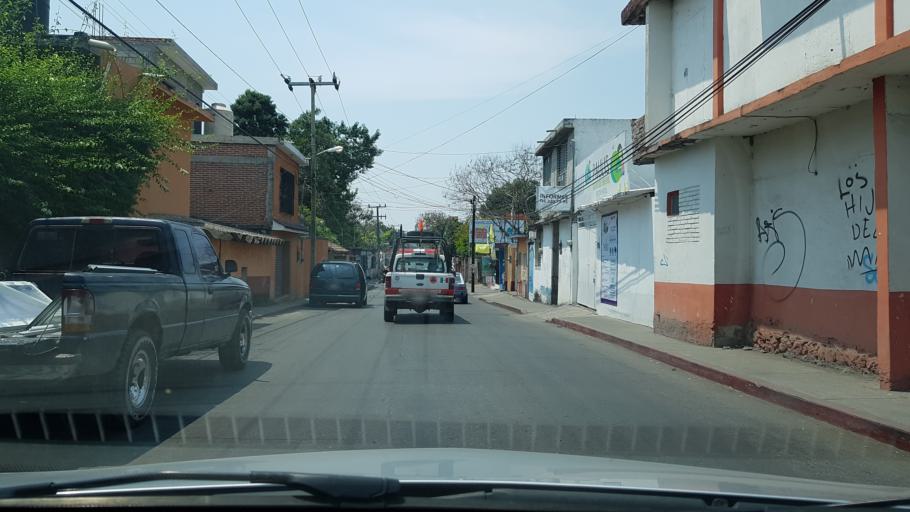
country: MX
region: Morelos
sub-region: Jiutepec
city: Jiutepec
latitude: 18.8855
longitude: -99.1770
